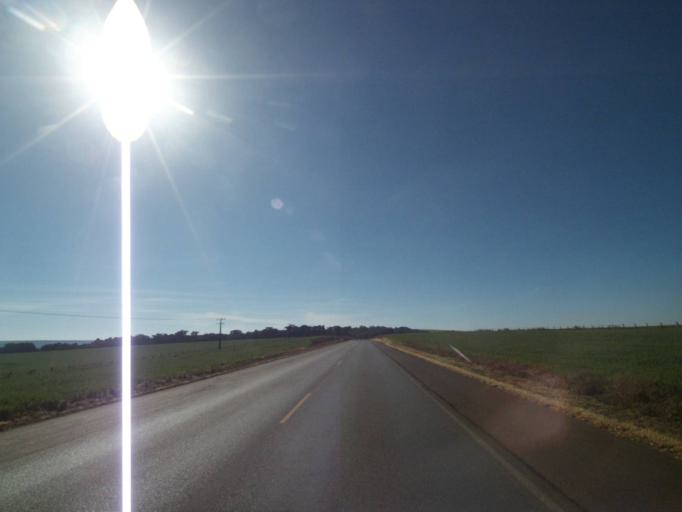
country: BR
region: Parana
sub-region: Tibagi
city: Tibagi
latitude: -24.4291
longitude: -50.4048
